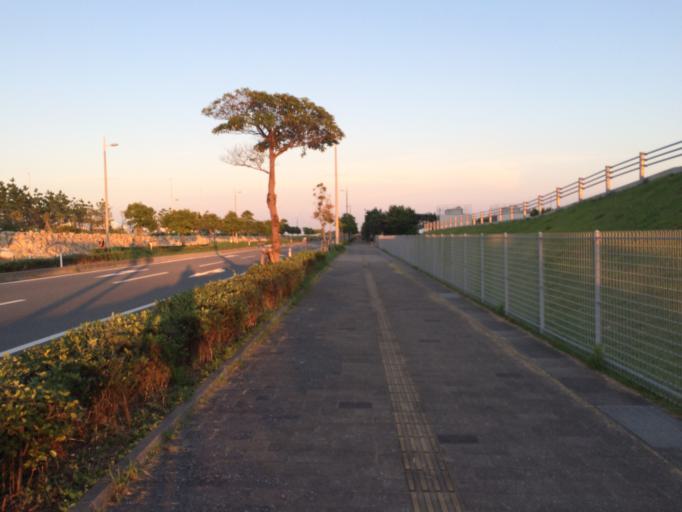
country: JP
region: Yamaguchi
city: Ogori-shimogo
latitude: 34.0093
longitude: 131.3731
